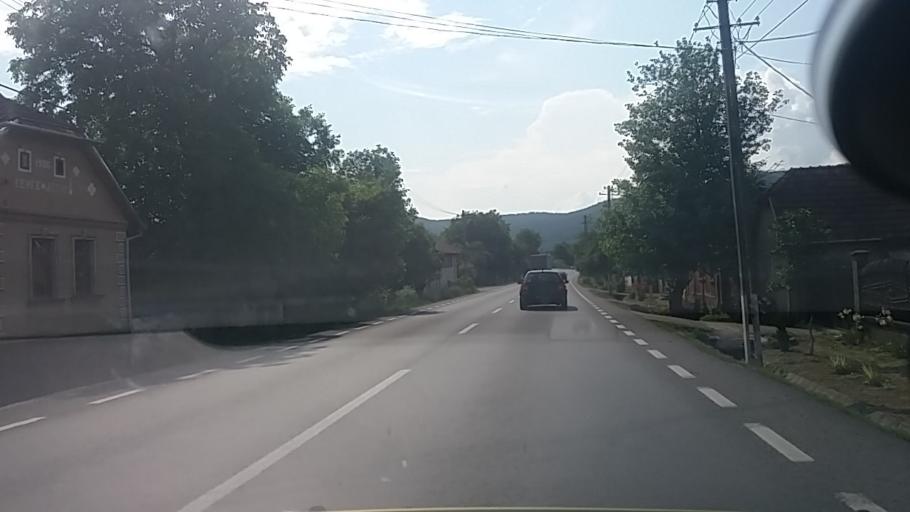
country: RO
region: Arad
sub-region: Comuna Barzava
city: Barzava
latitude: 46.1109
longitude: 21.9734
